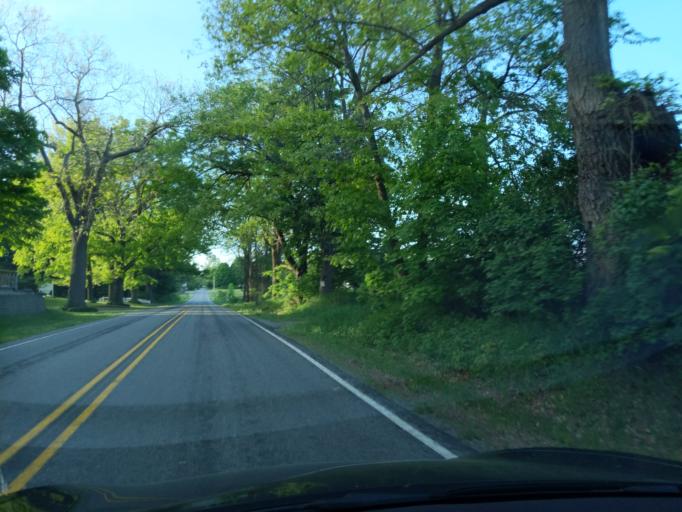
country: US
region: Michigan
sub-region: Ingham County
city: Leslie
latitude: 42.4721
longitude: -84.3169
